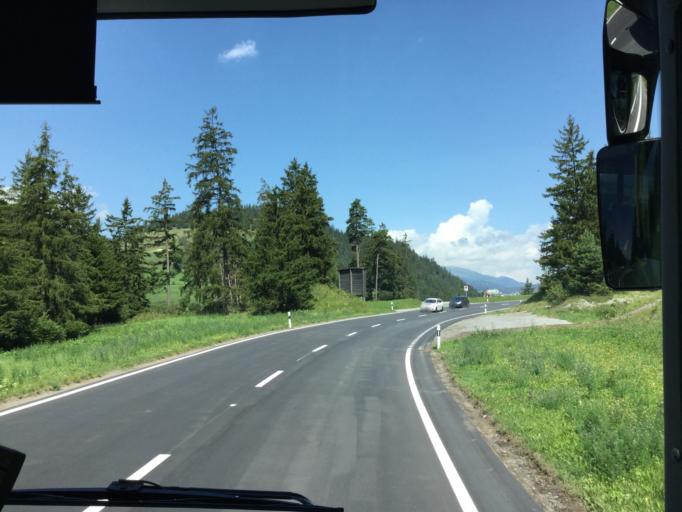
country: CH
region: Grisons
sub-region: Albula District
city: Tiefencastel
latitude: 46.6277
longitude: 9.5843
